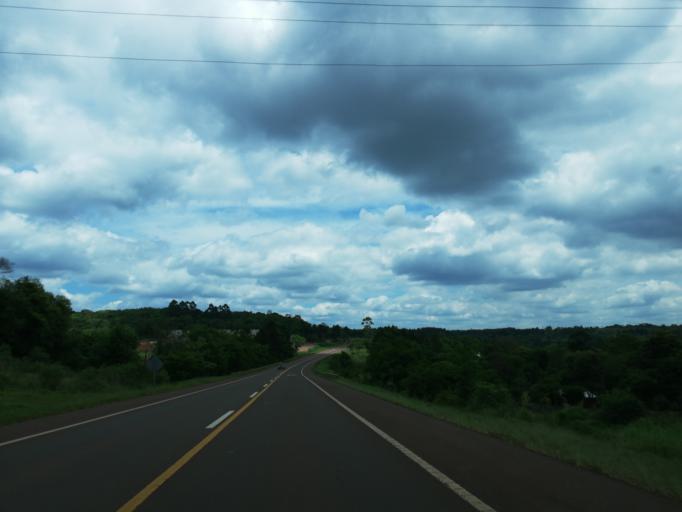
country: AR
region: Misiones
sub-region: Departamento de Leandro N. Alem
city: Leandro N. Alem
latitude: -27.6384
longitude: -55.3472
